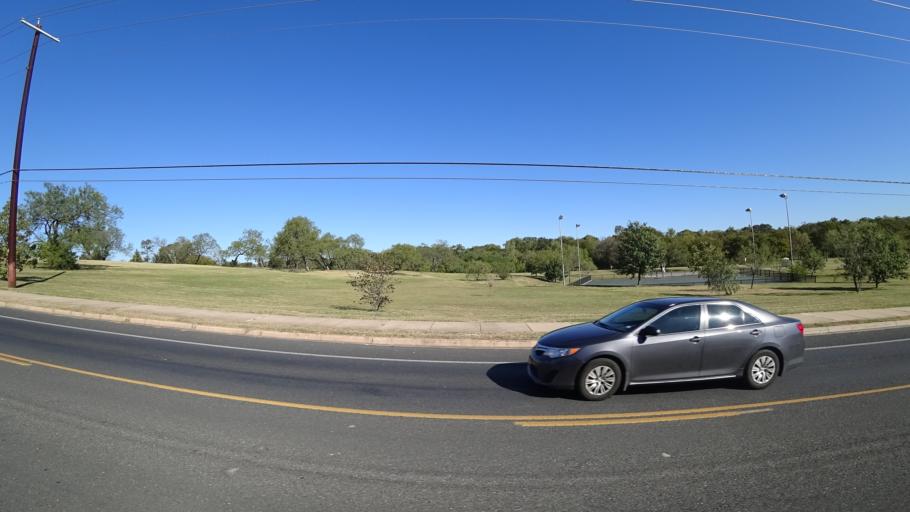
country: US
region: Texas
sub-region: Travis County
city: Austin
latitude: 30.3014
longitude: -97.6928
